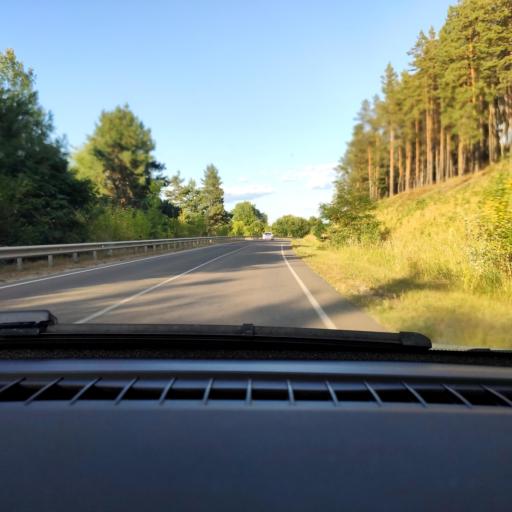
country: RU
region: Voronezj
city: Semiluki
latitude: 51.6732
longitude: 39.0264
